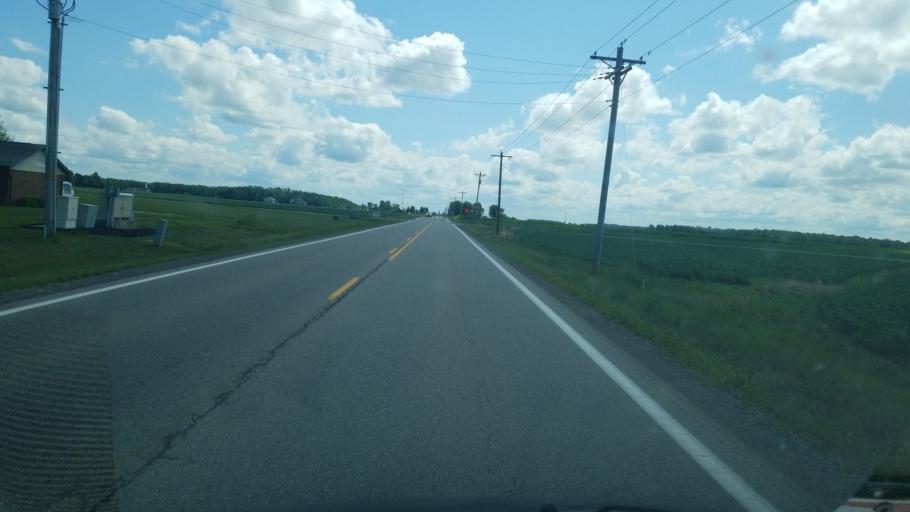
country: US
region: Ohio
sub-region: Putnam County
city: Kalida
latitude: 41.0292
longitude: -84.1981
